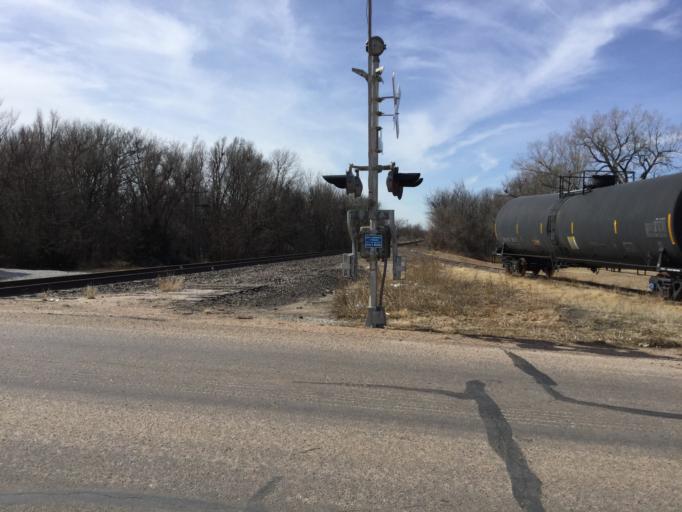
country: US
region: Kansas
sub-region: Barton County
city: Ellinwood
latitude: 38.5146
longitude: -98.3972
